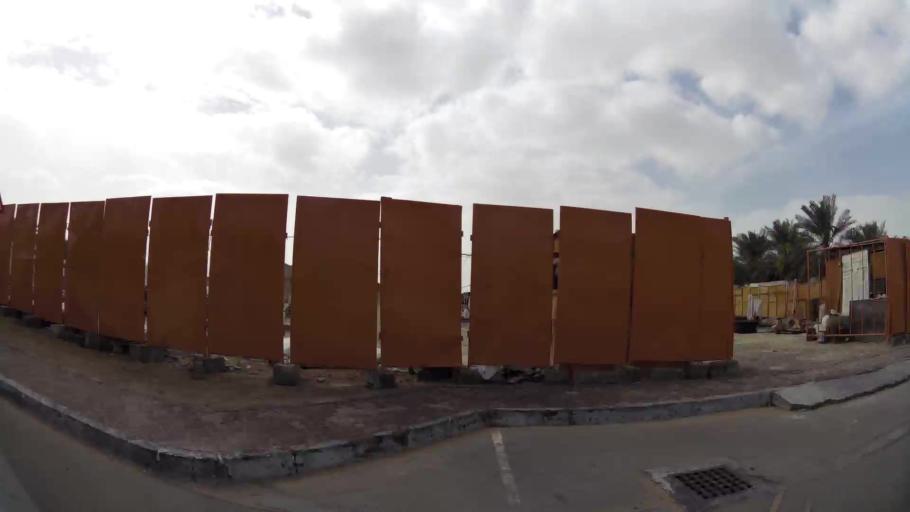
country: AE
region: Abu Dhabi
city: Abu Dhabi
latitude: 24.4013
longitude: 54.5090
